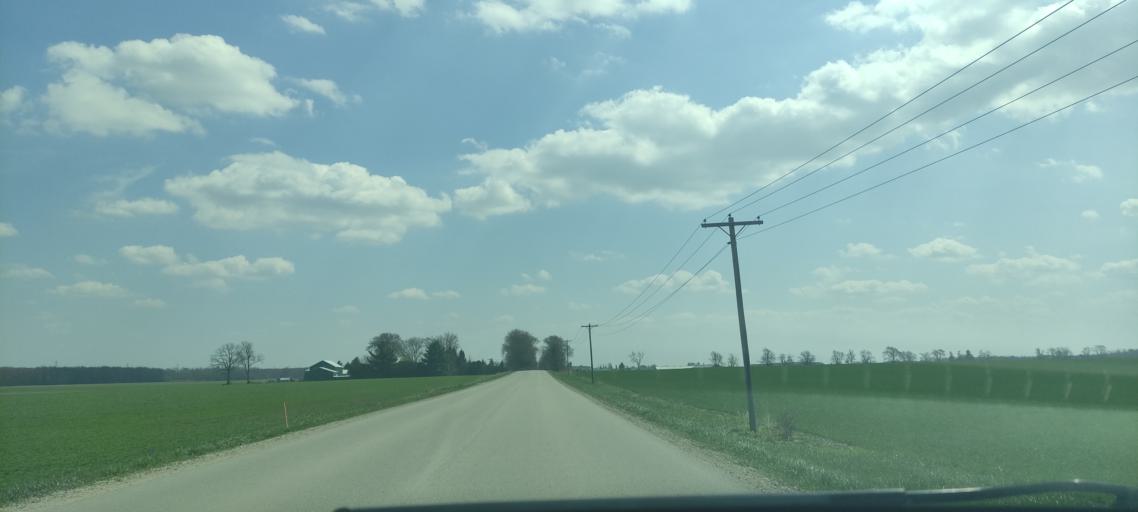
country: CA
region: Ontario
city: Stratford
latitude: 43.3351
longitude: -80.9890
